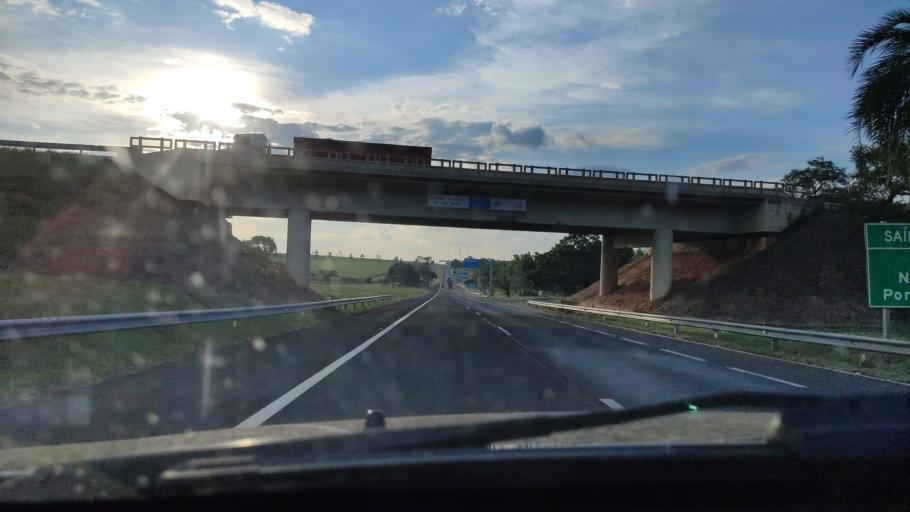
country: BR
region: Sao Paulo
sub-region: Rancharia
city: Rancharia
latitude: -22.4418
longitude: -50.9971
